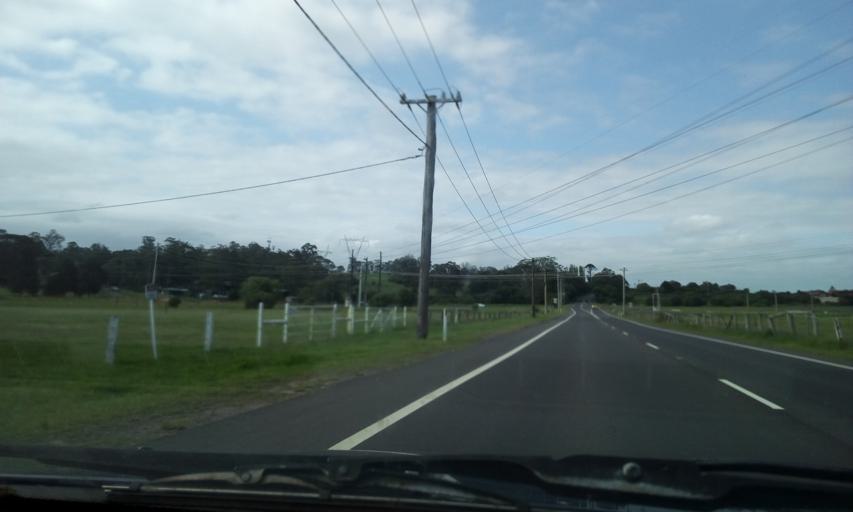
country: AU
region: New South Wales
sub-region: Campbelltown Municipality
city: Glen Alpine
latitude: -34.0955
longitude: 150.7687
